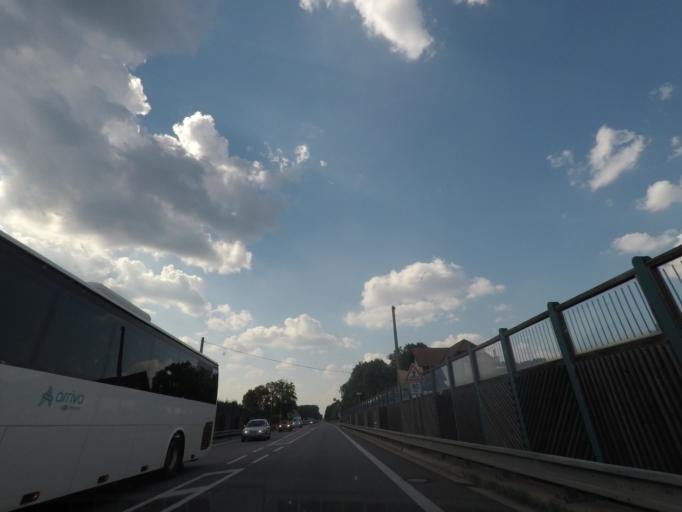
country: CZ
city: Albrechtice nad Orlici
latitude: 50.1723
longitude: 16.0369
